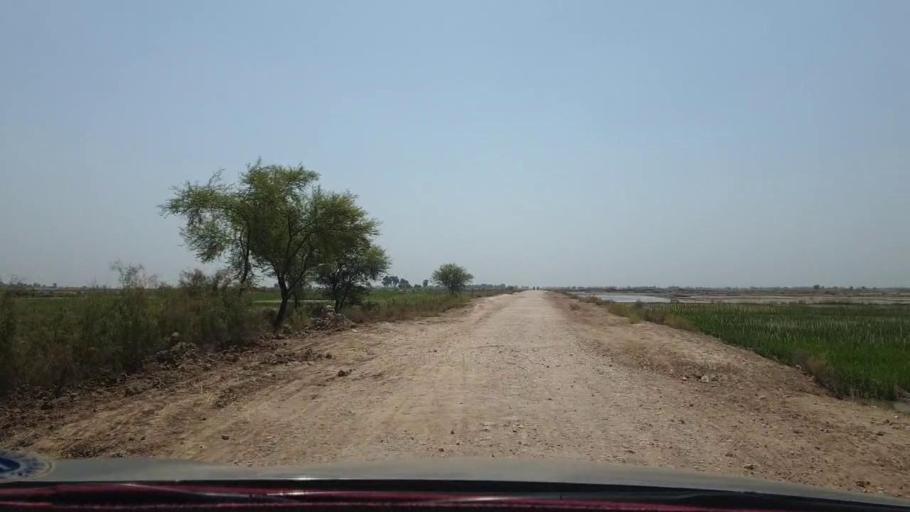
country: PK
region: Sindh
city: Kambar
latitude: 27.5863
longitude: 67.8760
